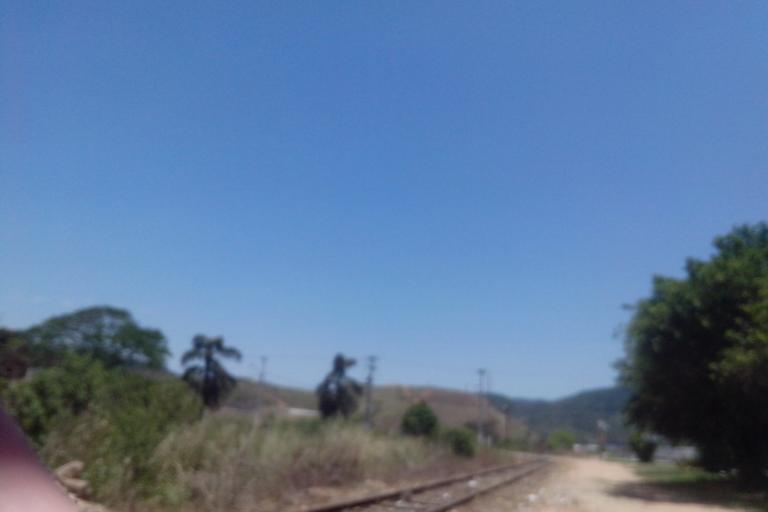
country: BR
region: Rio de Janeiro
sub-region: Rio Bonito
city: Rio Bonito
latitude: -22.7081
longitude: -42.6472
